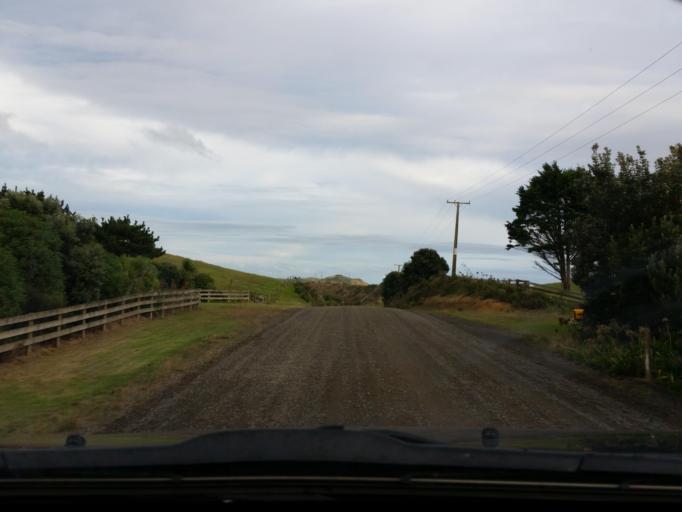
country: NZ
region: Northland
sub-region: Kaipara District
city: Dargaville
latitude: -35.8477
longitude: 173.6622
